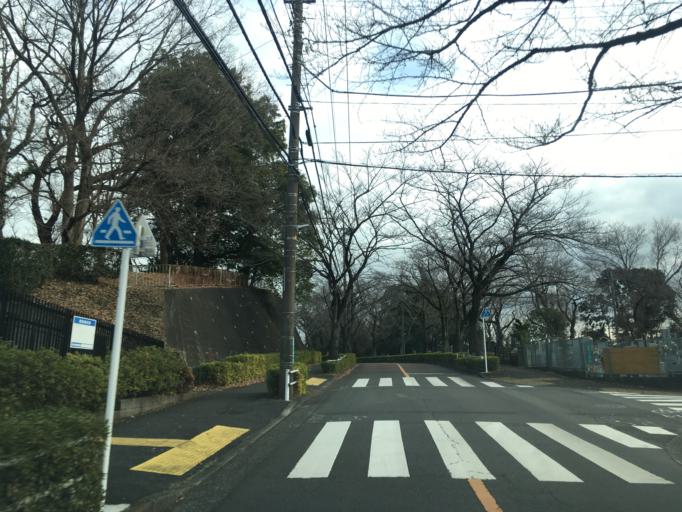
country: JP
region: Tokyo
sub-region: Machida-shi
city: Machida
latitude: 35.6079
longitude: 139.4305
